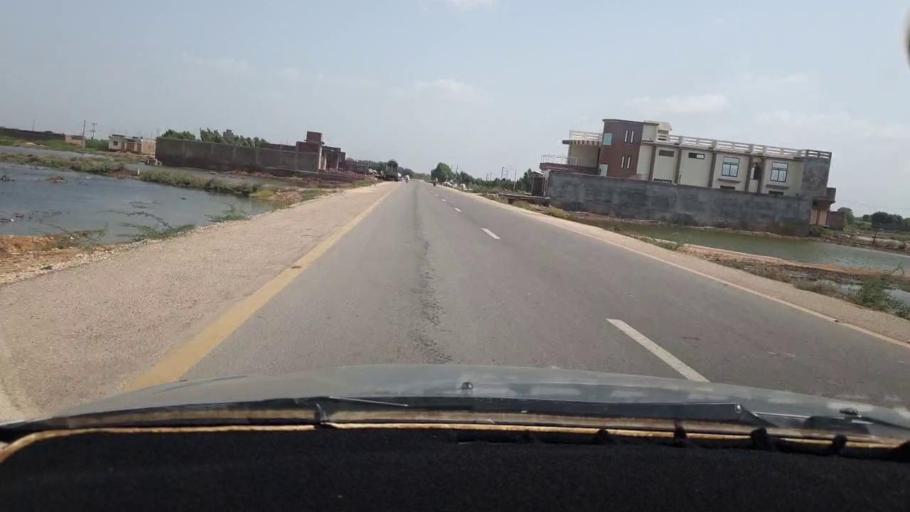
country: PK
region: Sindh
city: Digri
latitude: 25.1596
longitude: 69.1188
